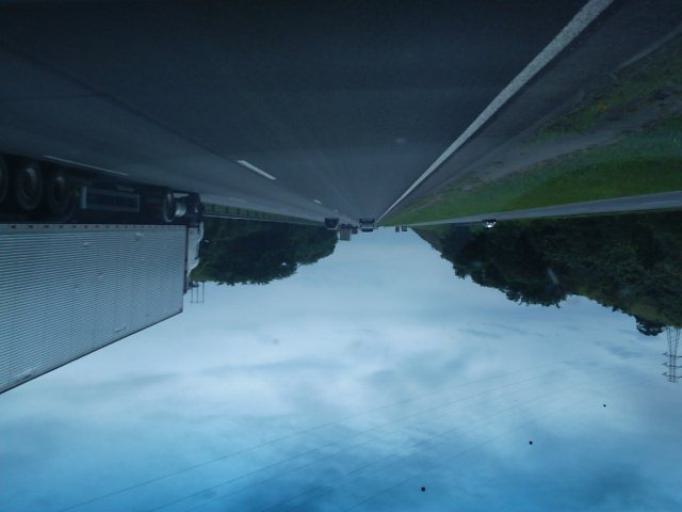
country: BR
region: Sao Paulo
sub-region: Juquia
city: Juquia
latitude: -24.3325
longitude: -47.6054
